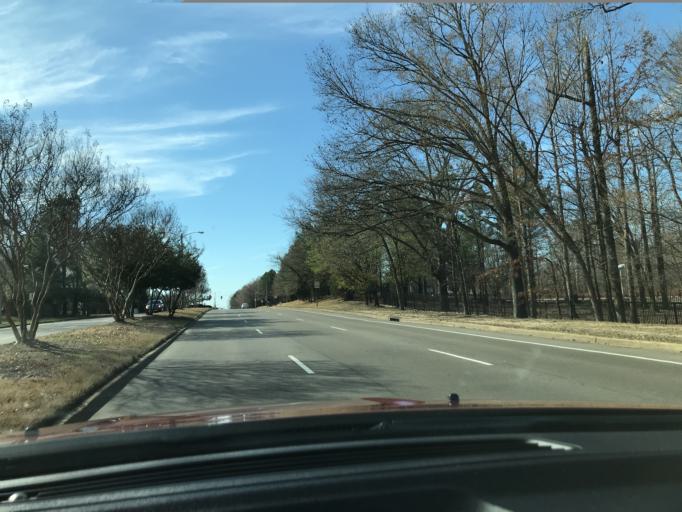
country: US
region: Tennessee
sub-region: Shelby County
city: Germantown
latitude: 35.0482
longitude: -89.7876
